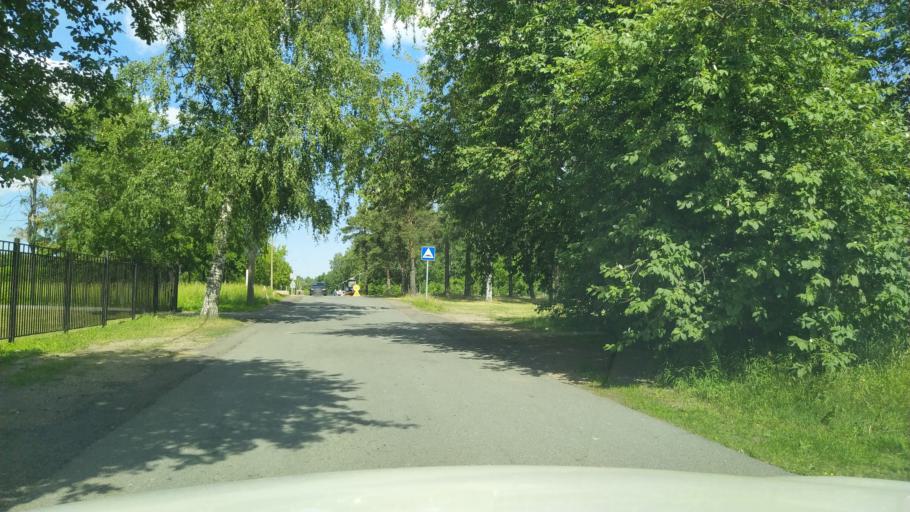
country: RU
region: Leningrad
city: Kalininskiy
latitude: 59.9957
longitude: 30.4137
